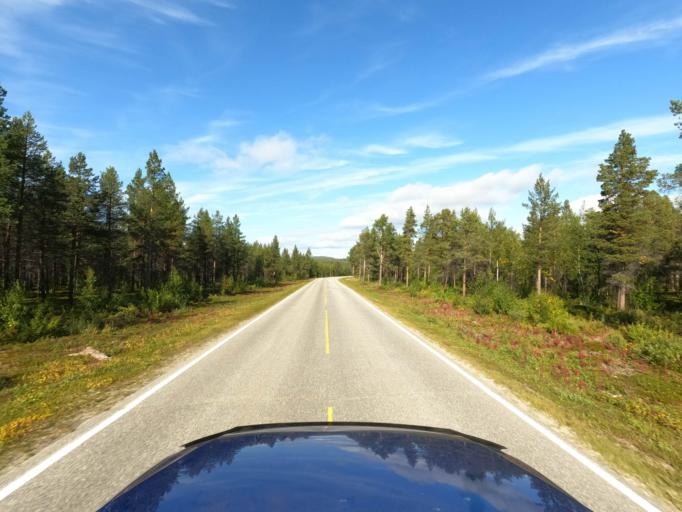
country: NO
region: Finnmark Fylke
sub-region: Porsanger
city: Lakselv
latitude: 69.8160
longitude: 25.1582
